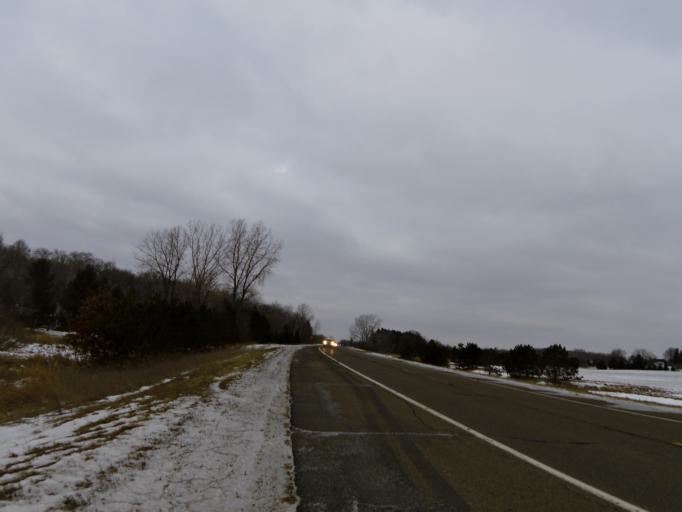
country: US
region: Minnesota
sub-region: Washington County
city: Lake Elmo
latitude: 44.9638
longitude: -92.8490
